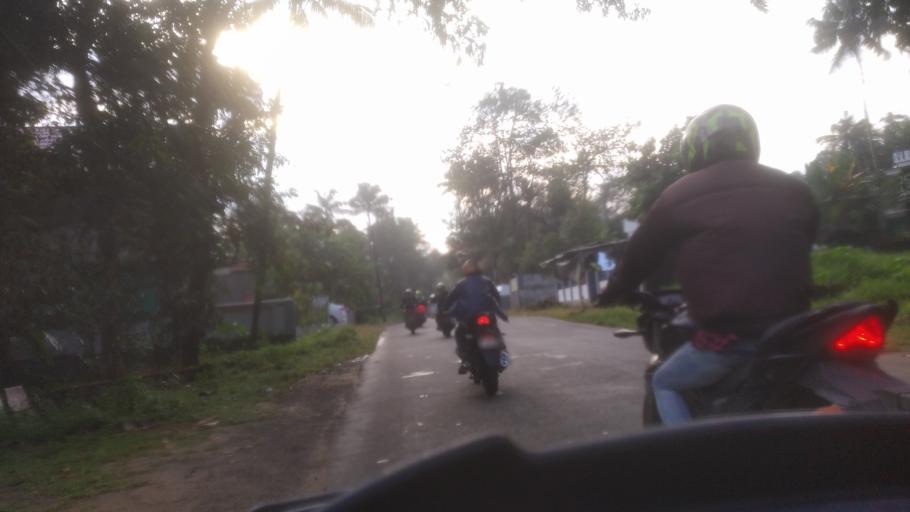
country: IN
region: Kerala
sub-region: Ernakulam
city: Perumpavur
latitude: 10.1039
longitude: 76.5394
